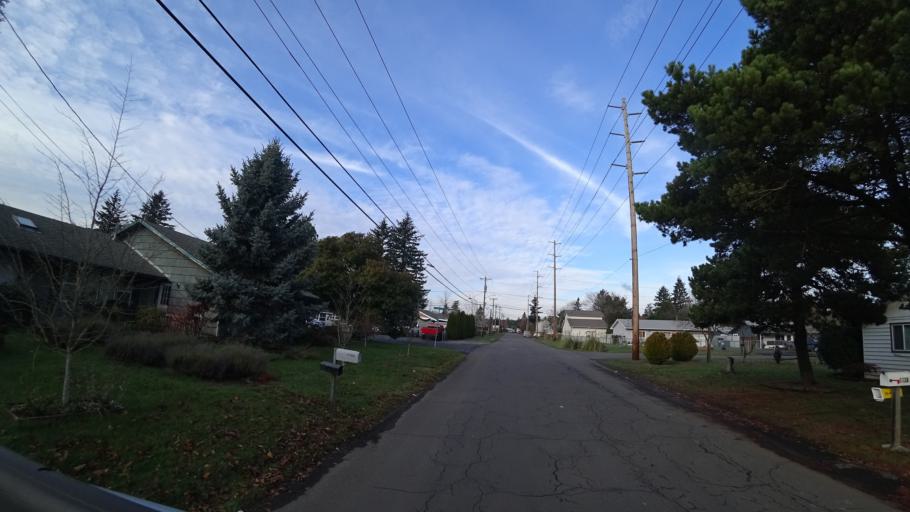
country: US
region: Oregon
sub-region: Multnomah County
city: Lents
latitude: 45.5311
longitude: -122.5312
